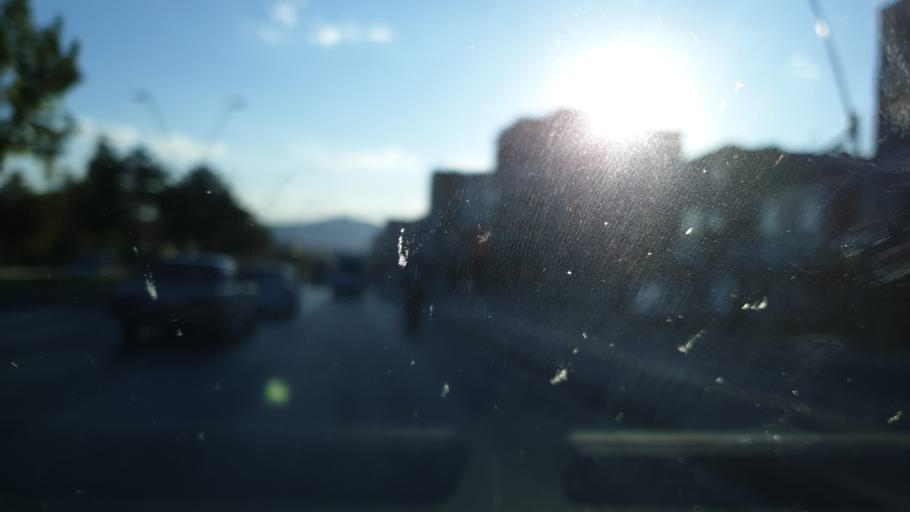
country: TR
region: Kayseri
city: Kayseri
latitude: 38.7444
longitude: 35.5269
